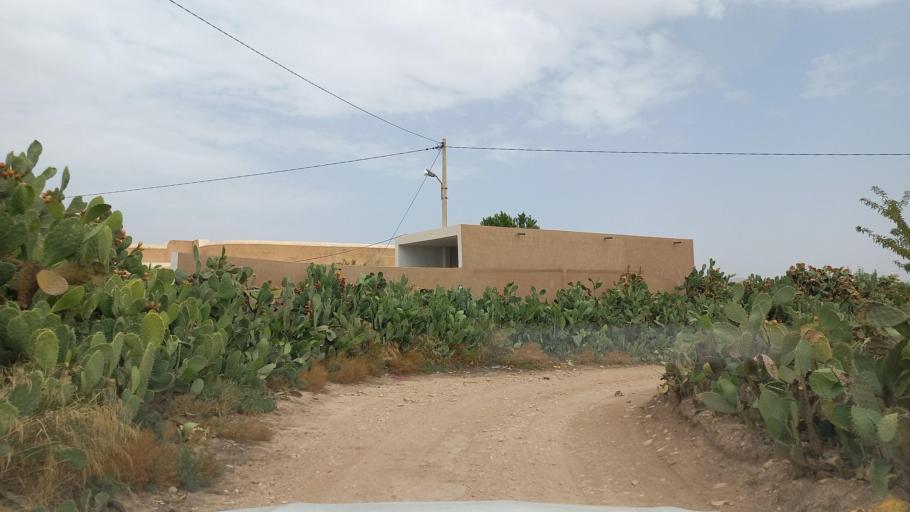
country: TN
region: Al Qasrayn
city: Kasserine
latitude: 35.2836
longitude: 9.0217
